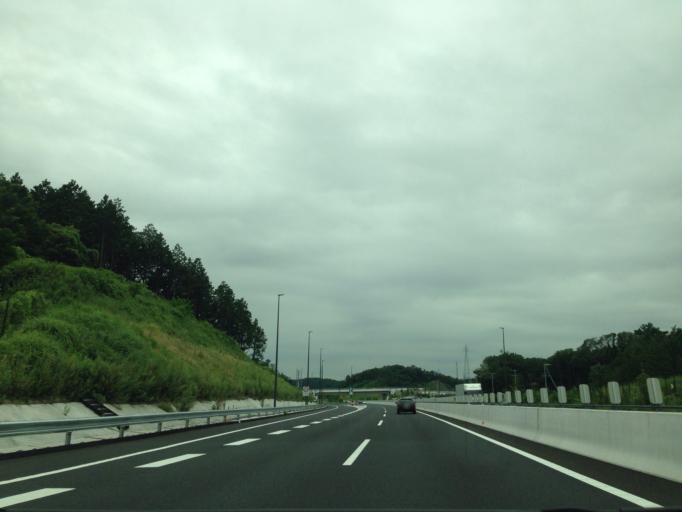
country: JP
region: Aichi
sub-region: Toyota-shi
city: Toyota
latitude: 35.0281
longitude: 137.2235
